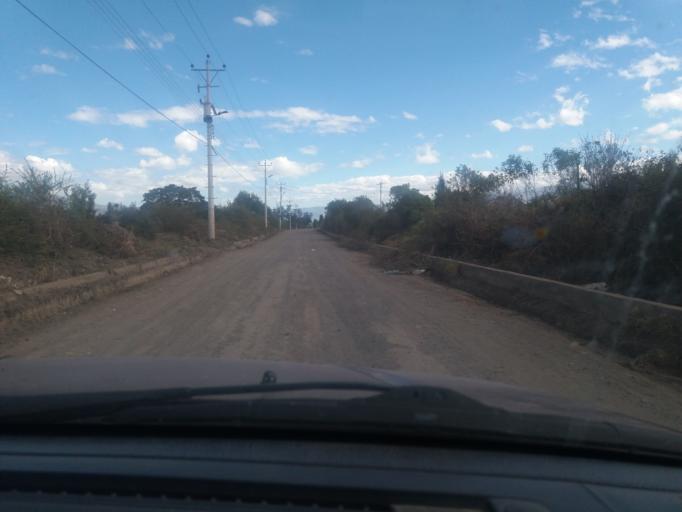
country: EC
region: Pichincha
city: Sangolqui
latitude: -0.1833
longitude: -78.3357
